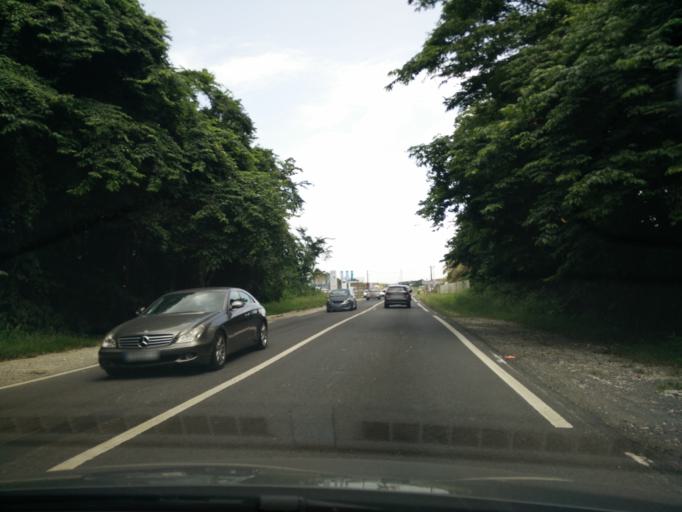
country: GP
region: Guadeloupe
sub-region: Guadeloupe
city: Baie-Mahault
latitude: 16.2493
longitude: -61.5711
